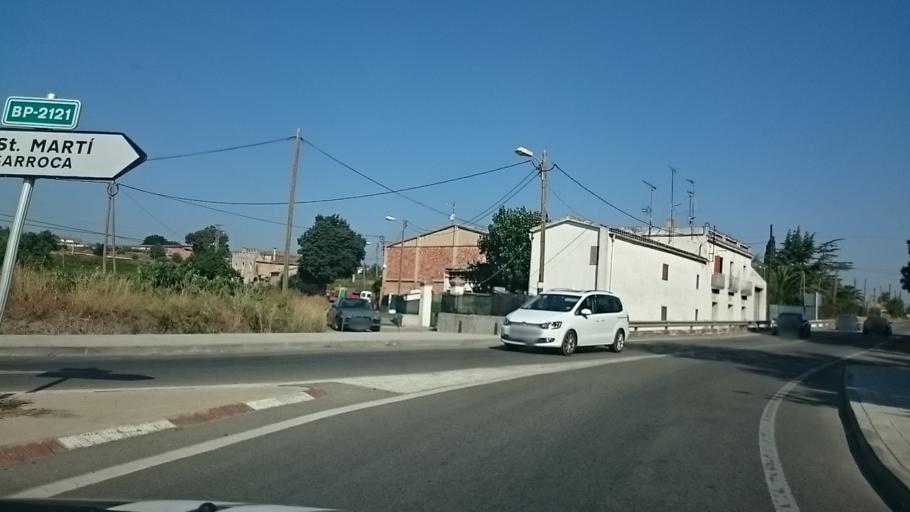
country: ES
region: Catalonia
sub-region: Provincia de Barcelona
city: Vilafranca del Penedes
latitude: 41.3549
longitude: 1.6674
